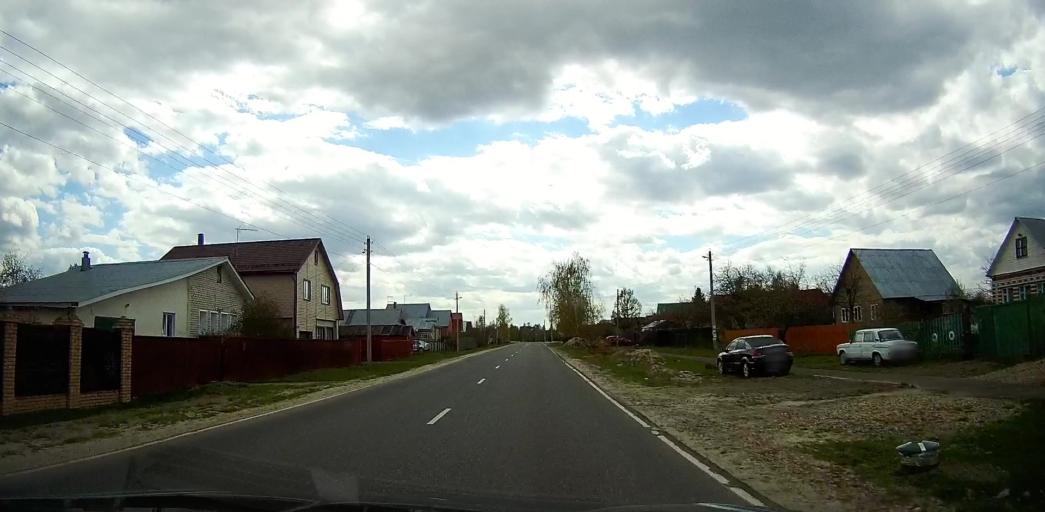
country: RU
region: Moskovskaya
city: Drezna
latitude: 55.6659
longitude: 38.7604
